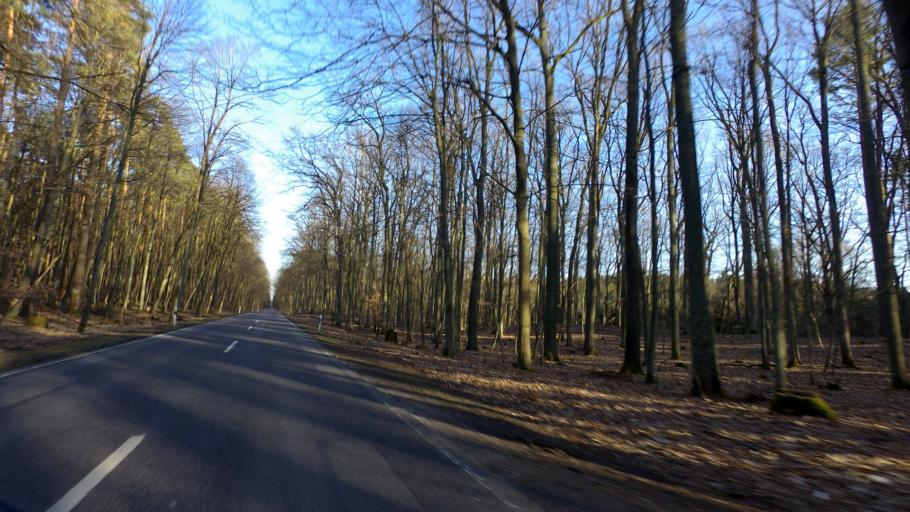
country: DE
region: Brandenburg
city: Joachimsthal
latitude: 52.9543
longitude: 13.7635
